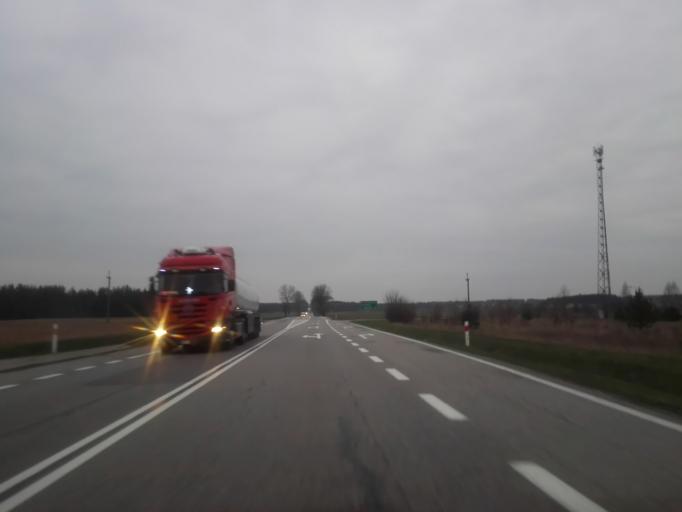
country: PL
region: Podlasie
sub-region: Powiat kolnenski
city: Stawiski
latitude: 53.3237
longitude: 22.1530
